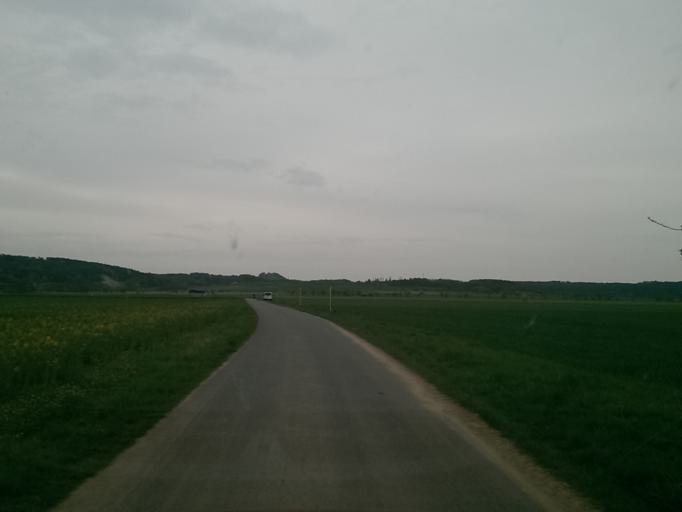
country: CZ
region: Central Bohemia
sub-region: Okres Mlada Boleslav
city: Zd'ar
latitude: 50.5576
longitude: 15.0860
